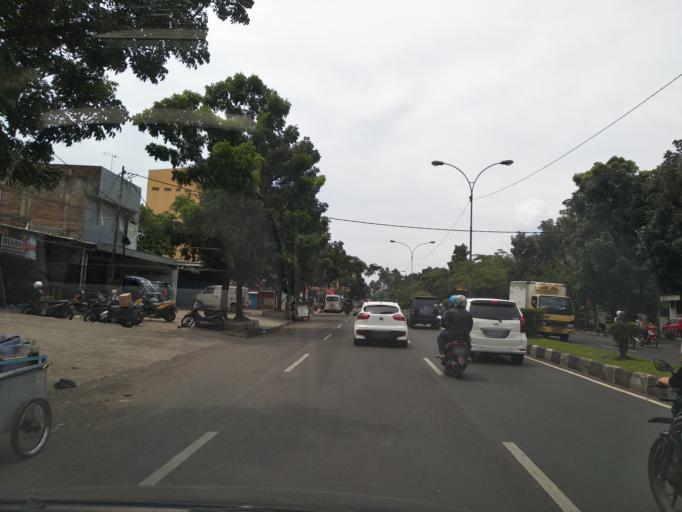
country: ID
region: West Java
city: Bandung
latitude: -6.9376
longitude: 107.5991
